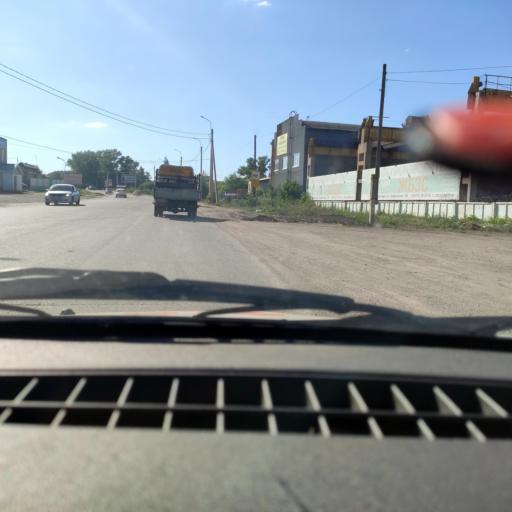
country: RU
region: Bashkortostan
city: Sterlitamak
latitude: 53.6523
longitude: 55.9739
